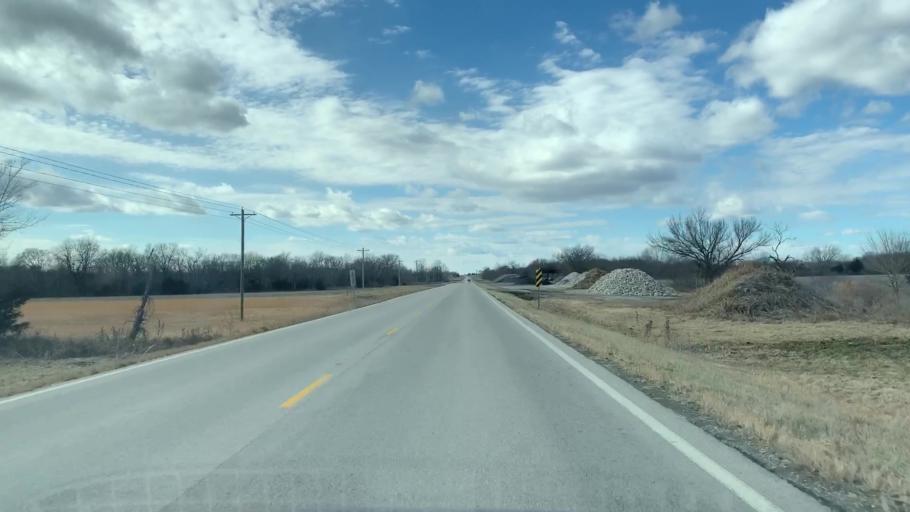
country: US
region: Kansas
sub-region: Neosho County
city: Erie
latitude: 37.5293
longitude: -95.2851
